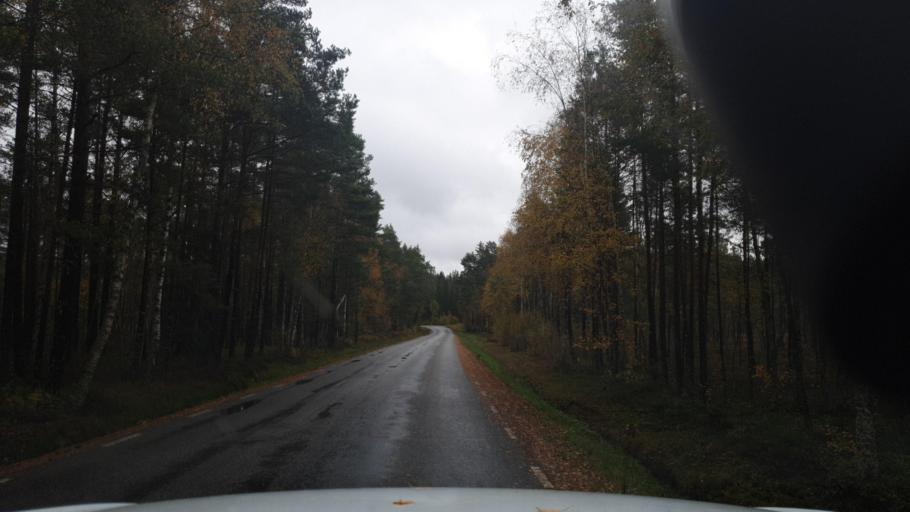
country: SE
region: Vaermland
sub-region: Karlstads Kommun
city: Valberg
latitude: 59.4167
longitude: 13.1399
